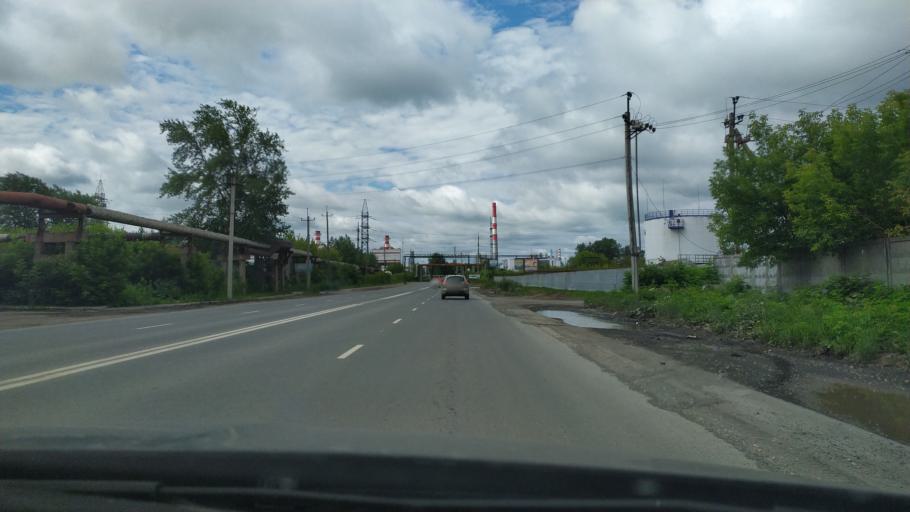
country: RU
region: Perm
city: Kondratovo
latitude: 57.9280
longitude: 56.1408
